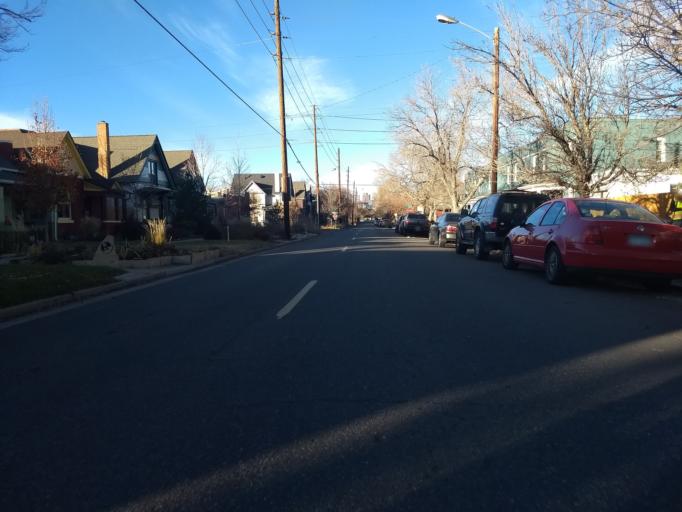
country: US
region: Colorado
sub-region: Denver County
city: Denver
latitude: 39.7141
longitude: -104.9900
